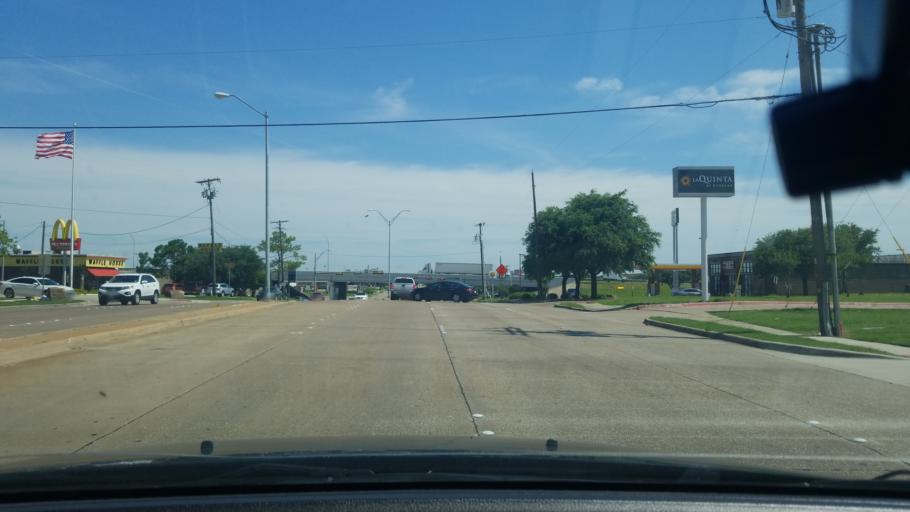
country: US
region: Texas
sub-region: Dallas County
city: Mesquite
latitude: 32.7887
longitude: -96.5957
